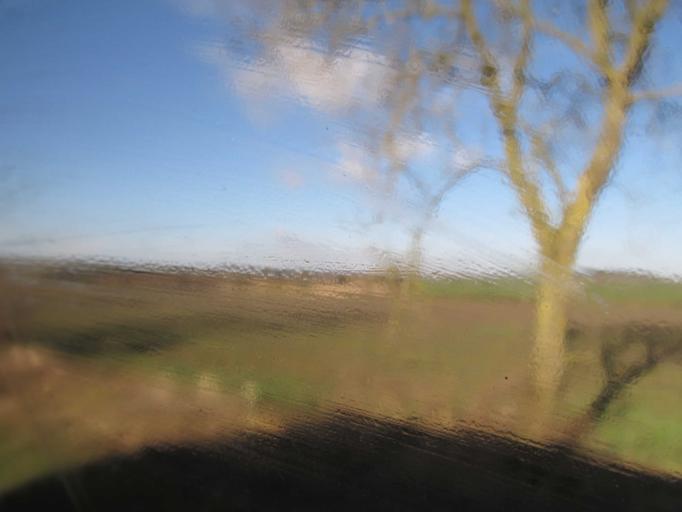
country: GB
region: England
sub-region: Hampshire
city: Kings Worthy
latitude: 51.1692
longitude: -1.3116
